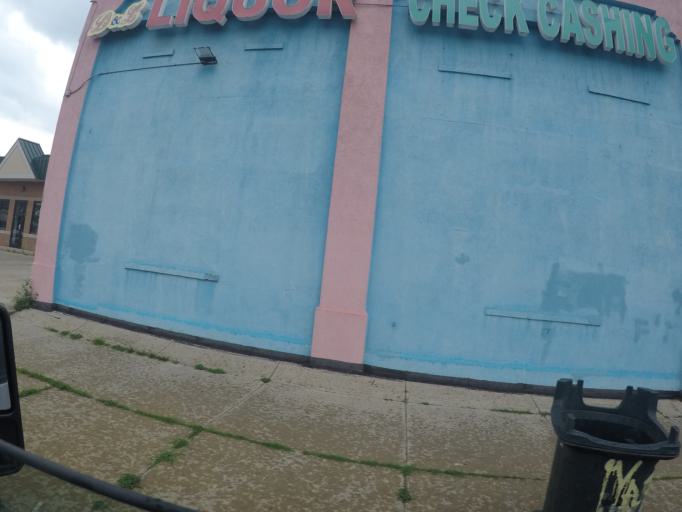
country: US
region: Michigan
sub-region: Wayne County
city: Highland Park
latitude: 42.3861
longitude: -83.1397
